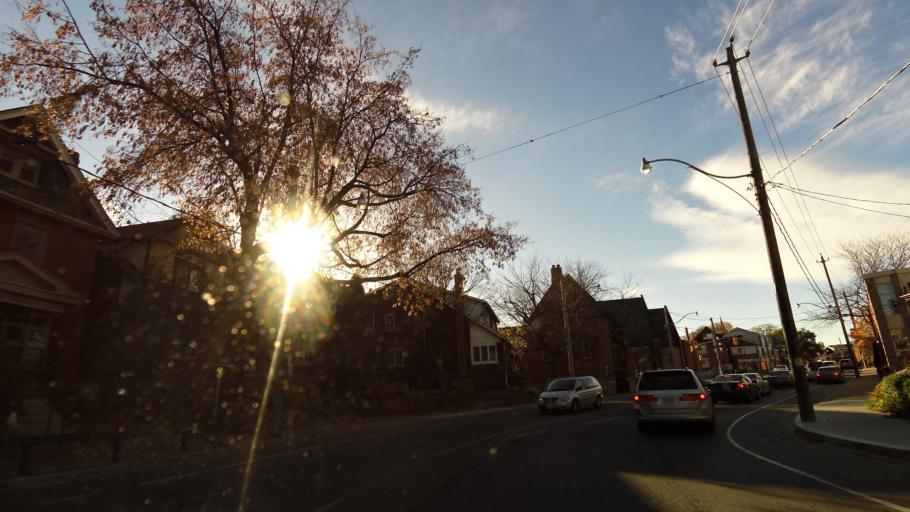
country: CA
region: Ontario
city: Toronto
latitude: 43.6635
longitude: -79.4626
